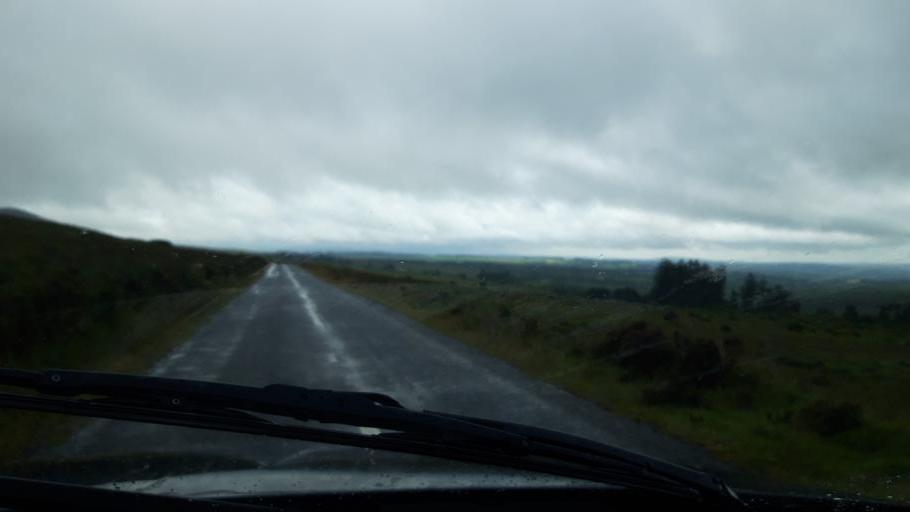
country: IE
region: Munster
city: Cahir
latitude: 52.2185
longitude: -7.9369
